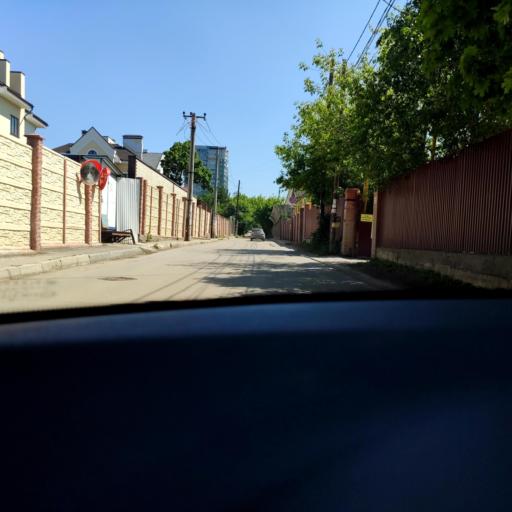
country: RU
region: Samara
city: Samara
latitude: 53.2359
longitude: 50.1748
